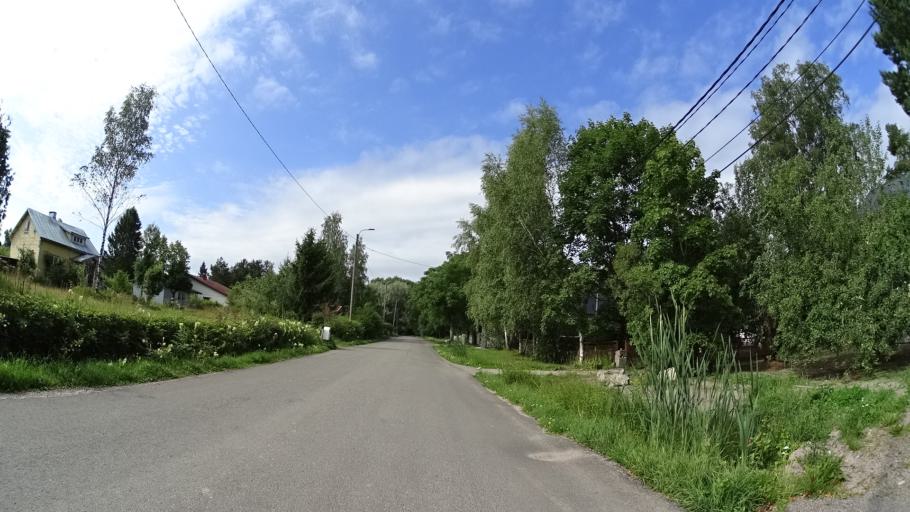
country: FI
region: Uusimaa
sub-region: Helsinki
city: Espoo
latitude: 60.1823
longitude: 24.5777
